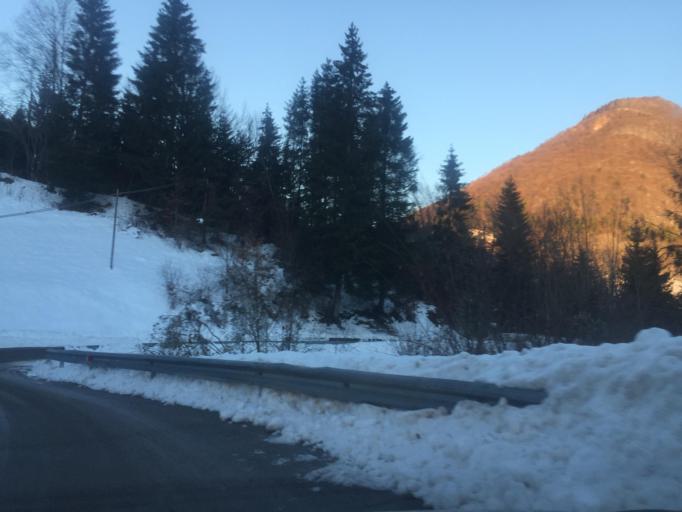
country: IT
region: Friuli Venezia Giulia
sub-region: Provincia di Udine
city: Lauco
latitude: 46.4376
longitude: 12.9488
